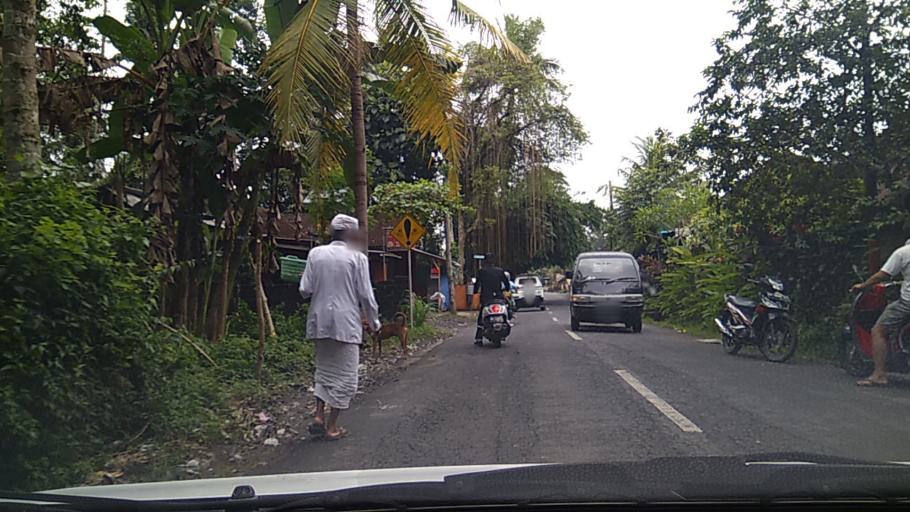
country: ID
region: Bali
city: Banjar Tebongkang
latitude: -8.5269
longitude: 115.2400
